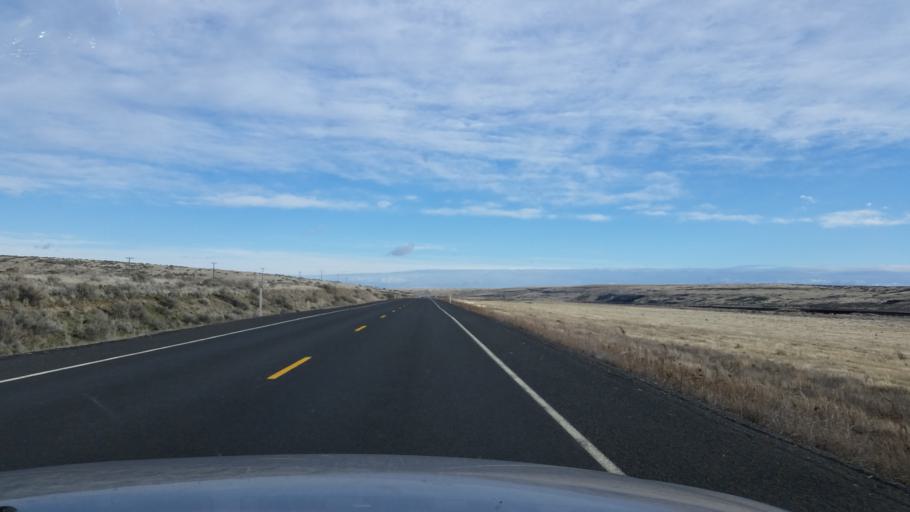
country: US
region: Washington
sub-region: Adams County
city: Ritzville
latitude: 47.3477
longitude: -118.5801
